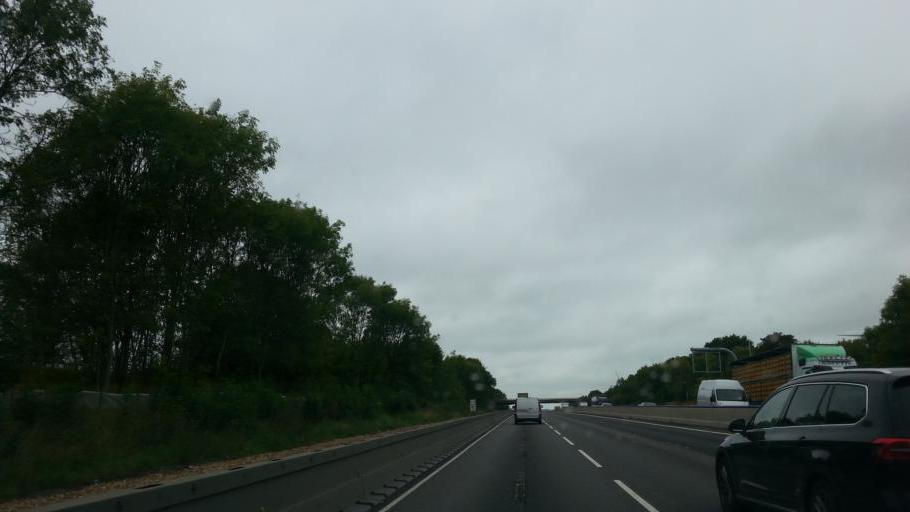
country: GB
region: England
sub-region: Northamptonshire
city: Long Buckby
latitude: 52.3647
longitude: -1.1590
